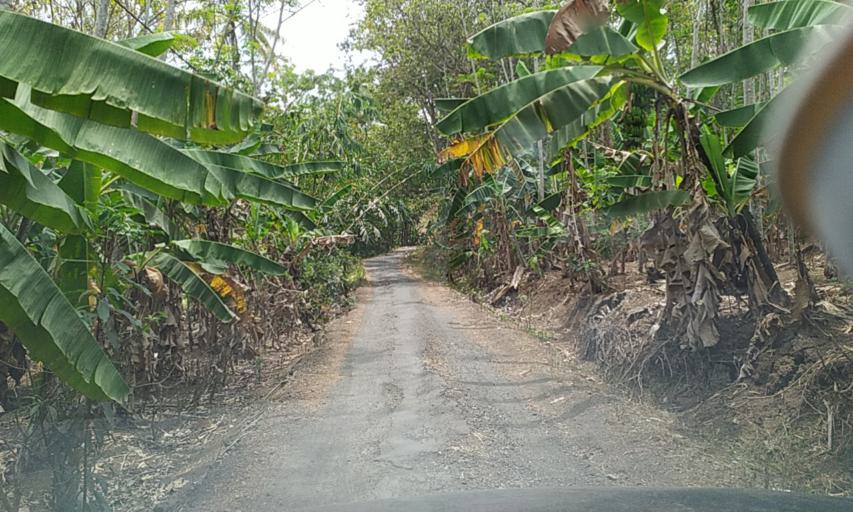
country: ID
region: Central Java
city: Sidakaya
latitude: -7.5671
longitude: 108.9233
